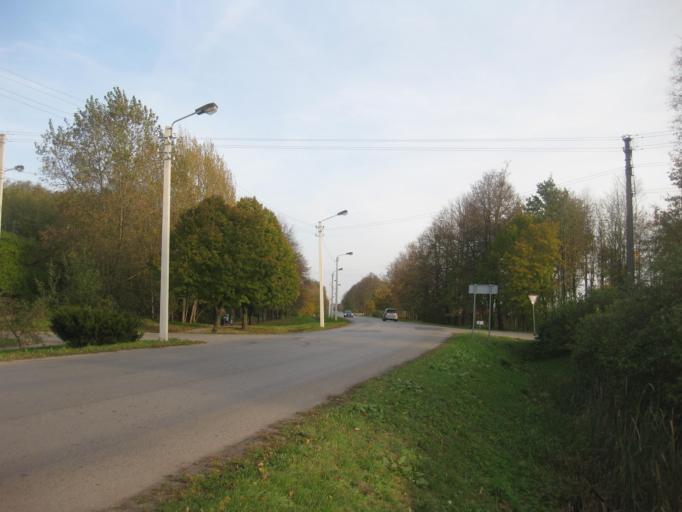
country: LT
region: Kauno apskritis
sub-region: Kaunas
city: Aleksotas
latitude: 54.8902
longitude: 23.8781
